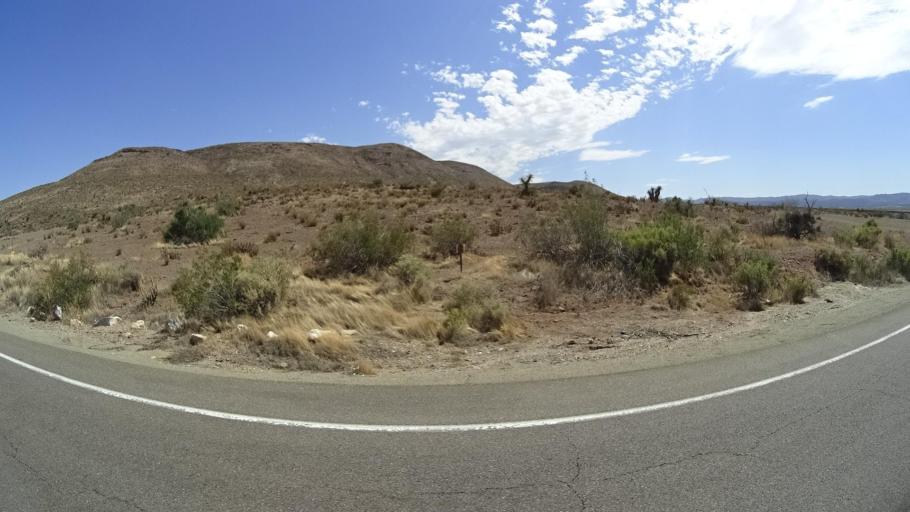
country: MX
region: Baja California
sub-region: Tecate
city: Cereso del Hongo
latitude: 32.6236
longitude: -116.1527
